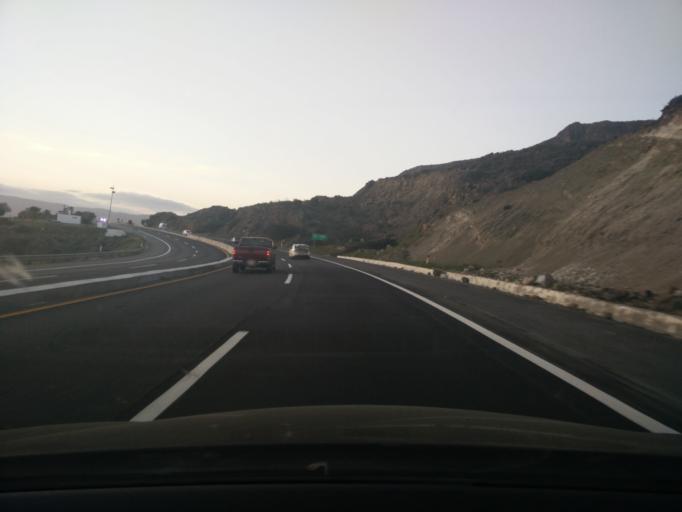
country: MX
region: Baja California
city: El Sauzal
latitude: 31.9287
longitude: -116.7522
